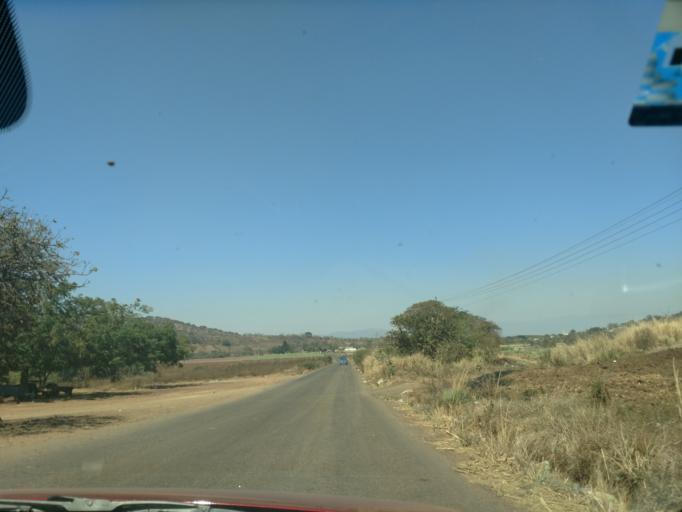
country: MX
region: Nayarit
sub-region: Tepic
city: La Corregidora
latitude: 21.5034
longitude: -104.7174
